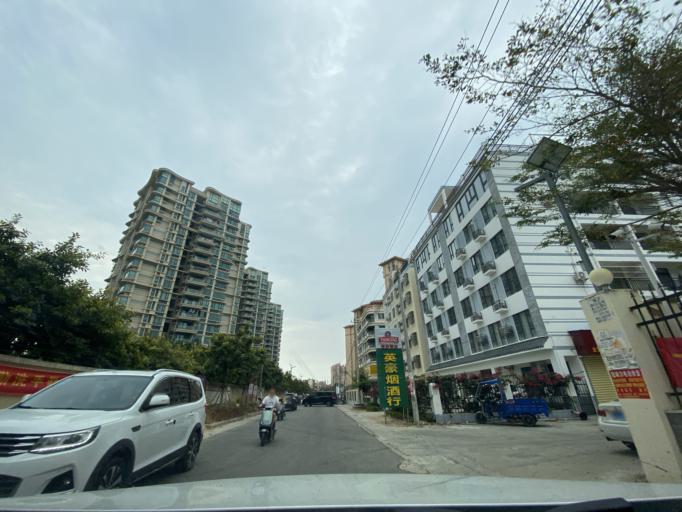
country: CN
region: Hainan
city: Yingzhou
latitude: 18.3986
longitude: 109.8439
